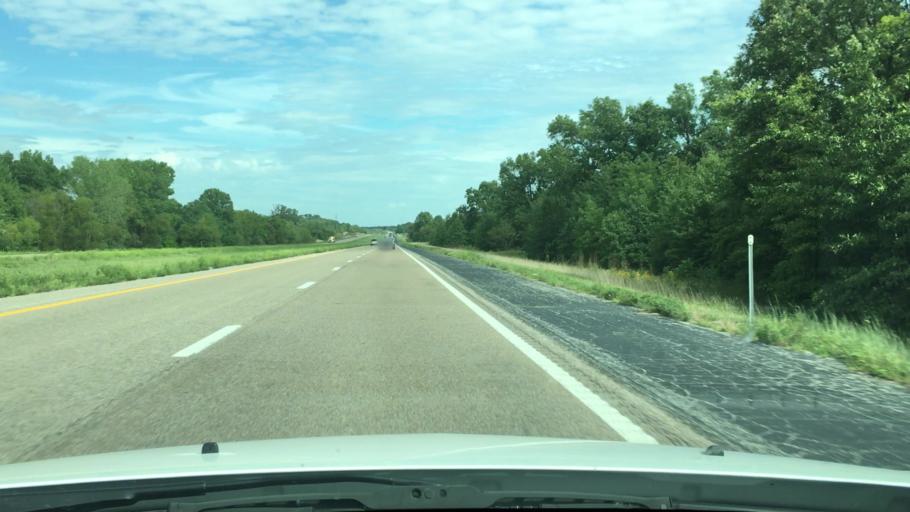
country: US
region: Missouri
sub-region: Audrain County
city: Mexico
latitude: 39.0430
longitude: -91.8933
